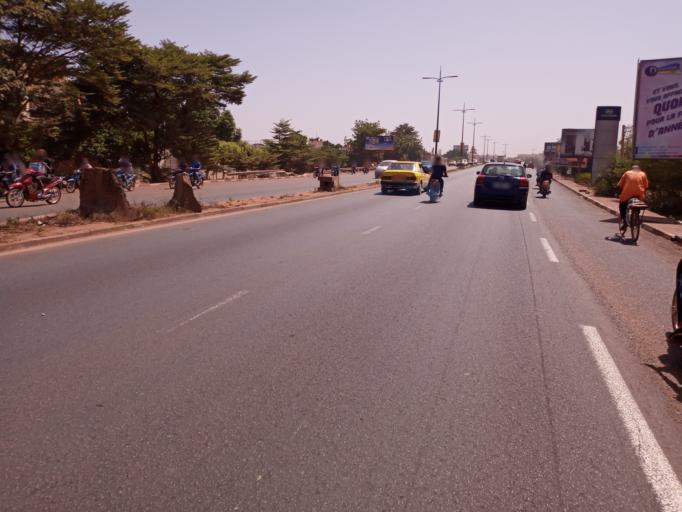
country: ML
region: Bamako
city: Bamako
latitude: 12.6170
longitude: -8.0003
